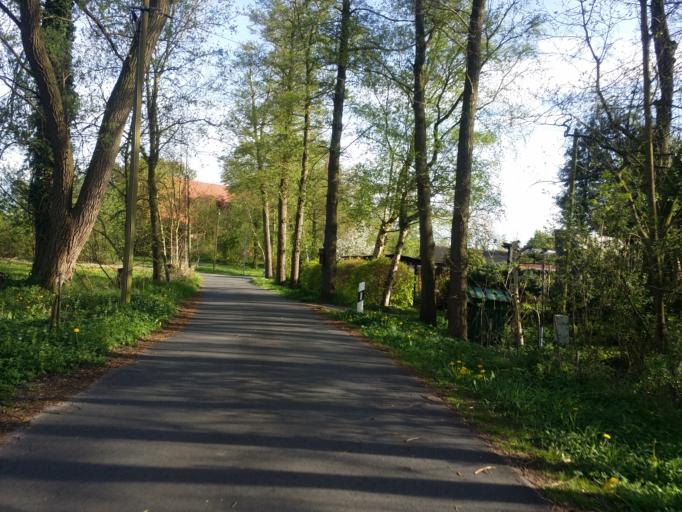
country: DE
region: Lower Saxony
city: Ritterhude
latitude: 53.1575
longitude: 8.7796
